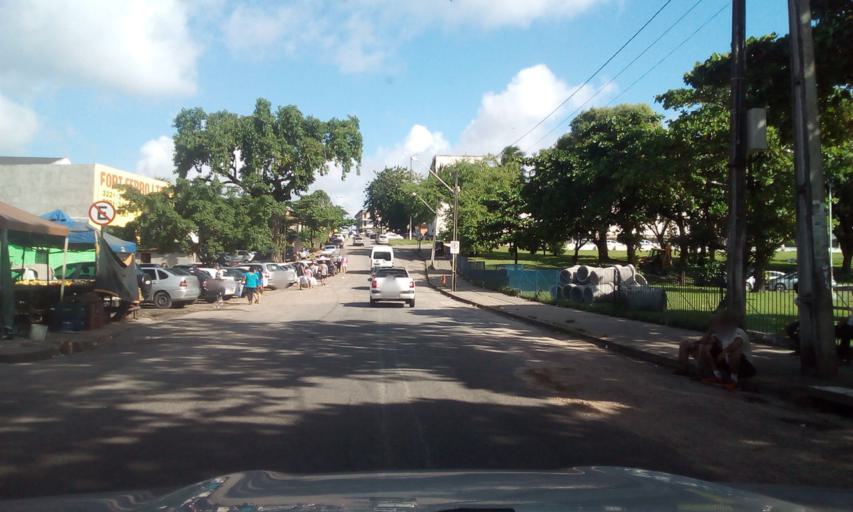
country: BR
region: Paraiba
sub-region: Joao Pessoa
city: Joao Pessoa
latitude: -7.1189
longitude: -34.8903
